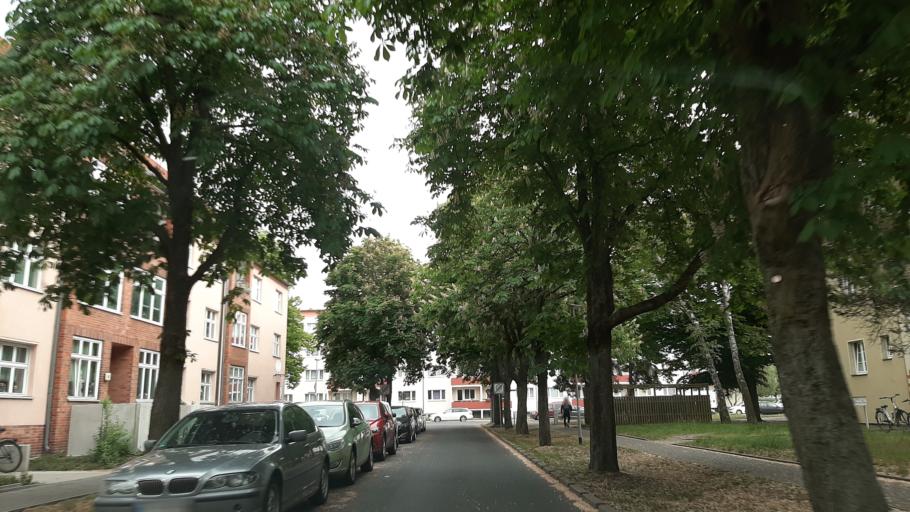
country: DE
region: Brandenburg
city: Hennigsdorf
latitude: 52.6406
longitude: 13.1991
